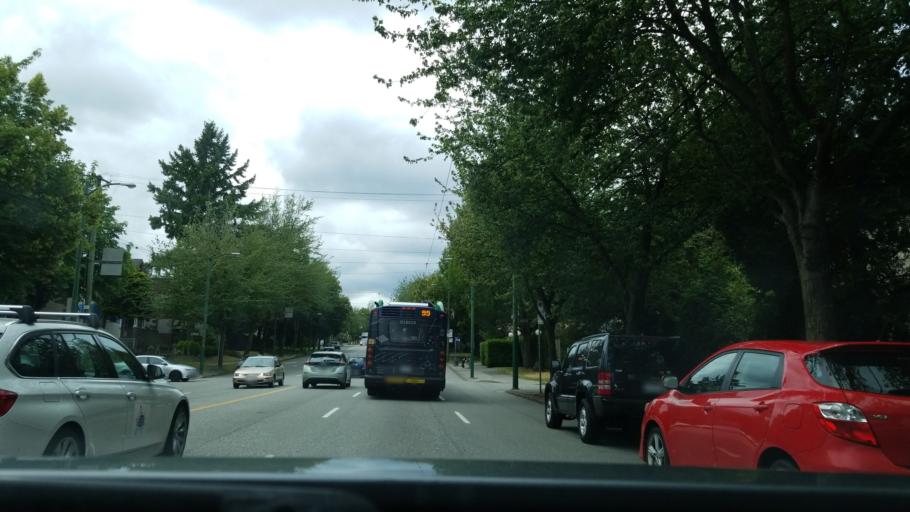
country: CA
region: British Columbia
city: Vancouver
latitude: 49.2625
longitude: -123.0827
